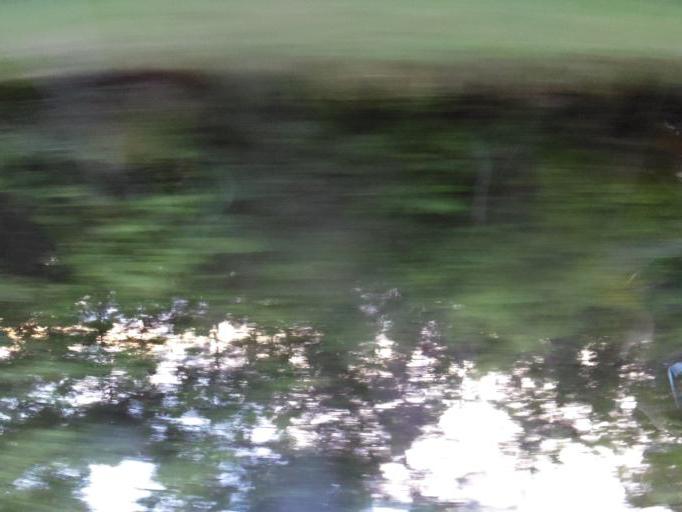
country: US
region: Georgia
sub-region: Echols County
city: Statenville
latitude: 30.7225
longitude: -83.0743
